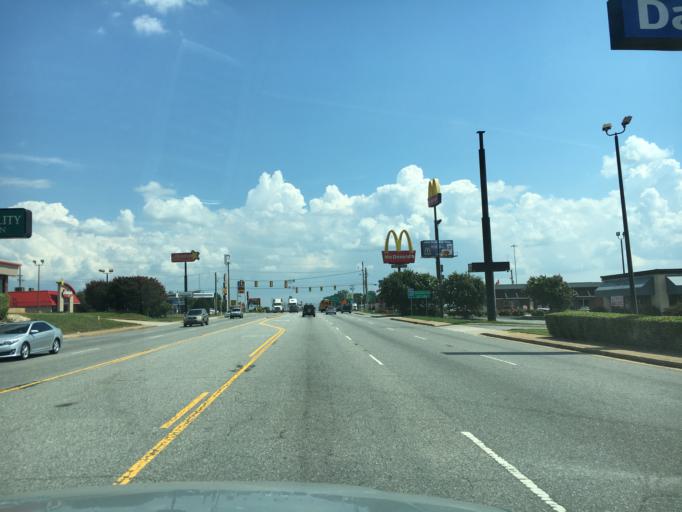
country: US
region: South Carolina
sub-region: Spartanburg County
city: Wellford
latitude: 34.9172
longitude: -82.1113
